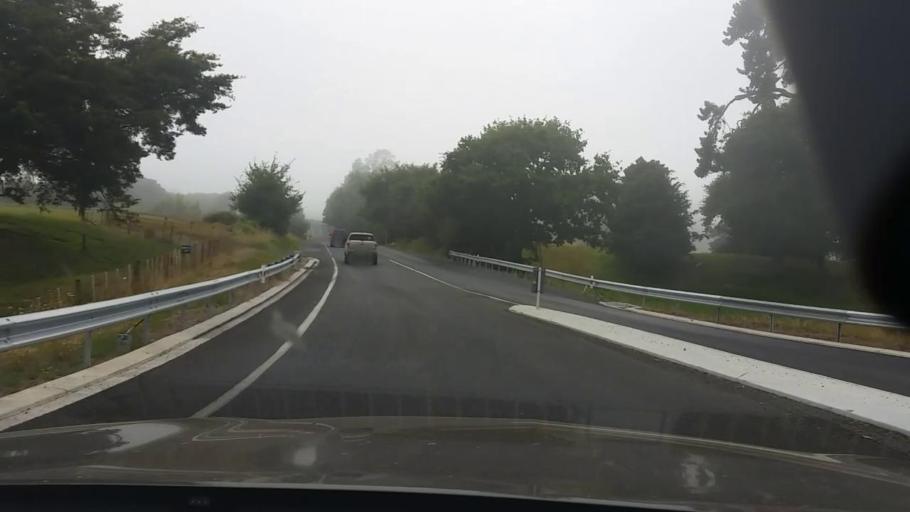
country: NZ
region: Waikato
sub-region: Hamilton City
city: Hamilton
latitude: -37.6550
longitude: 175.2922
